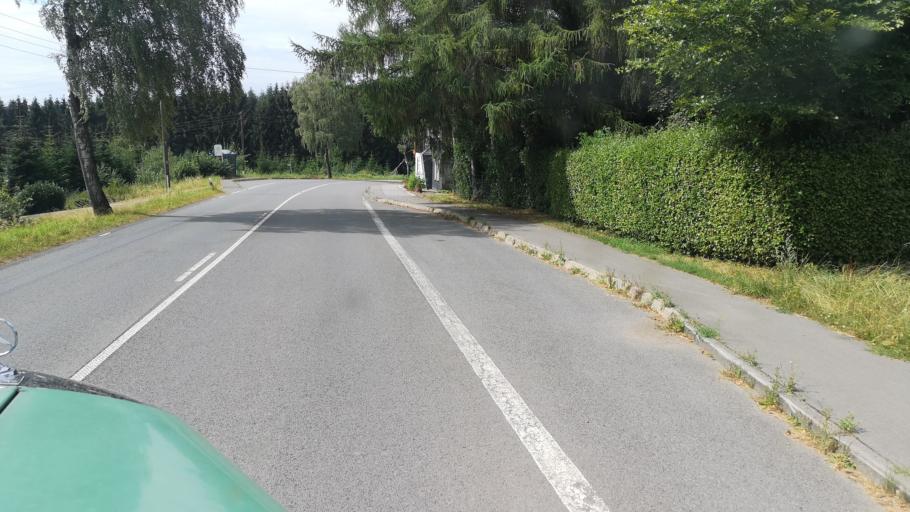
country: DE
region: North Rhine-Westphalia
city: Radevormwald
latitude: 51.1903
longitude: 7.3740
